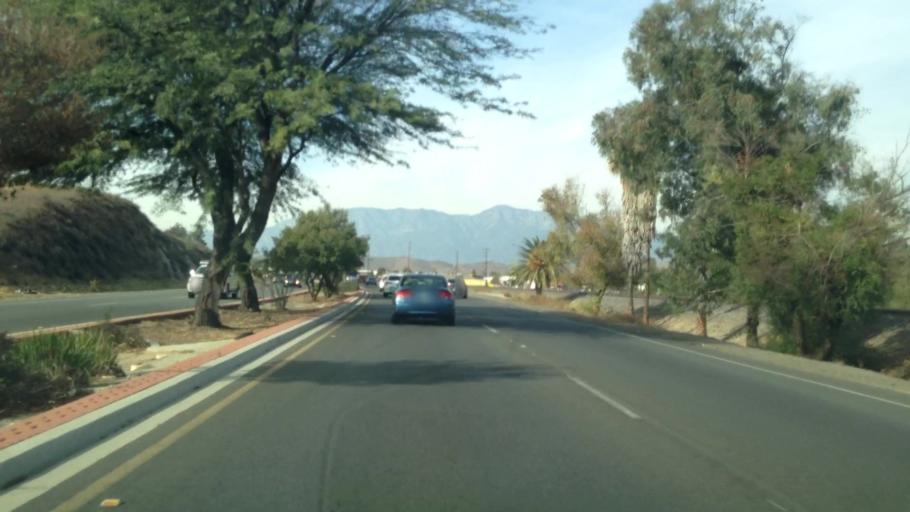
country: US
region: California
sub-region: Riverside County
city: Glen Avon
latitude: 33.9931
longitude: -117.4821
